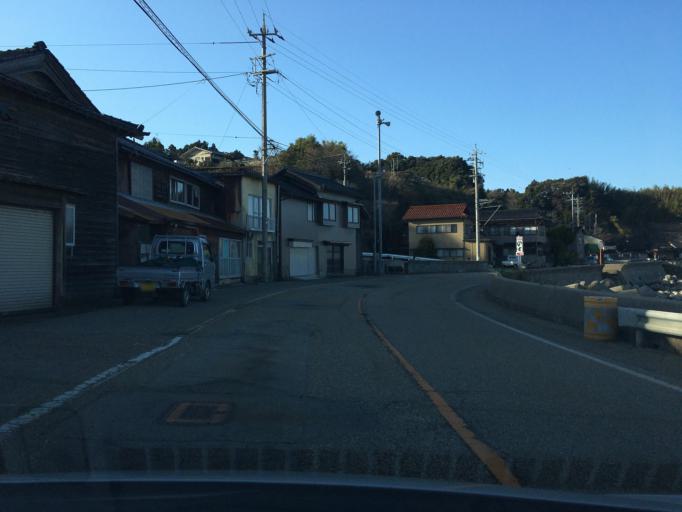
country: JP
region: Ishikawa
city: Nanao
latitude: 36.9603
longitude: 137.0514
